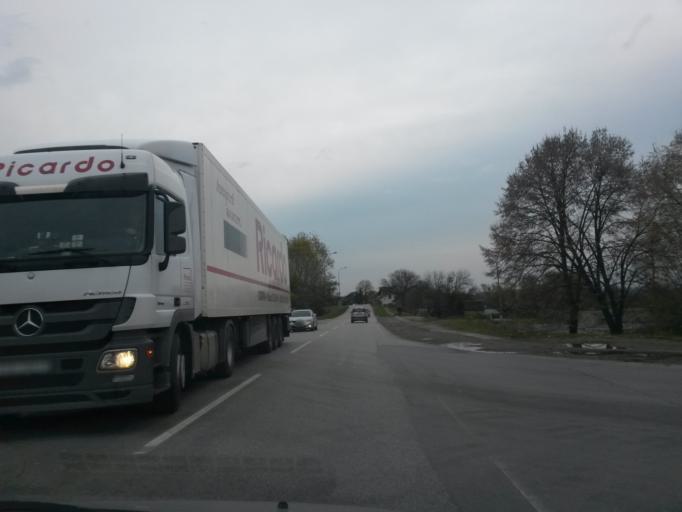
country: HR
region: Osjecko-Baranjska
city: Darda
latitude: 45.6238
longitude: 18.6992
